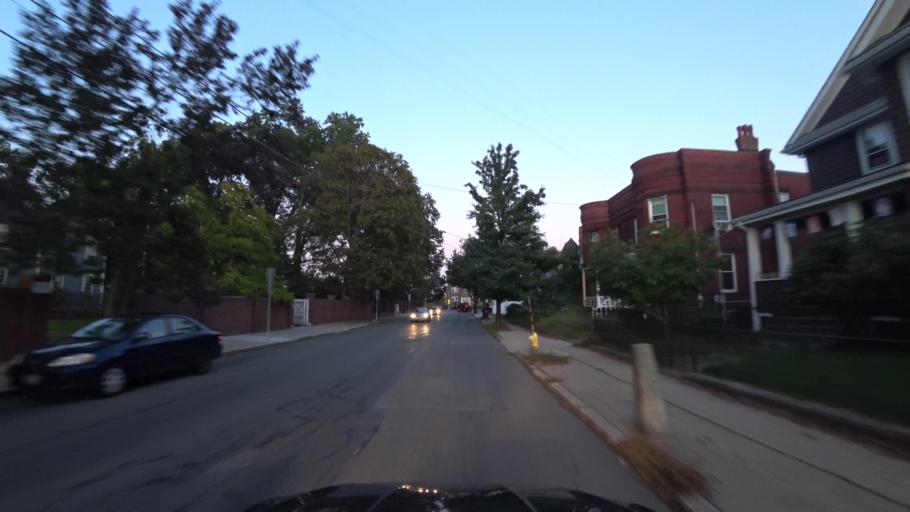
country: US
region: Massachusetts
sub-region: Middlesex County
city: Medford
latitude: 42.4121
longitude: -71.1121
